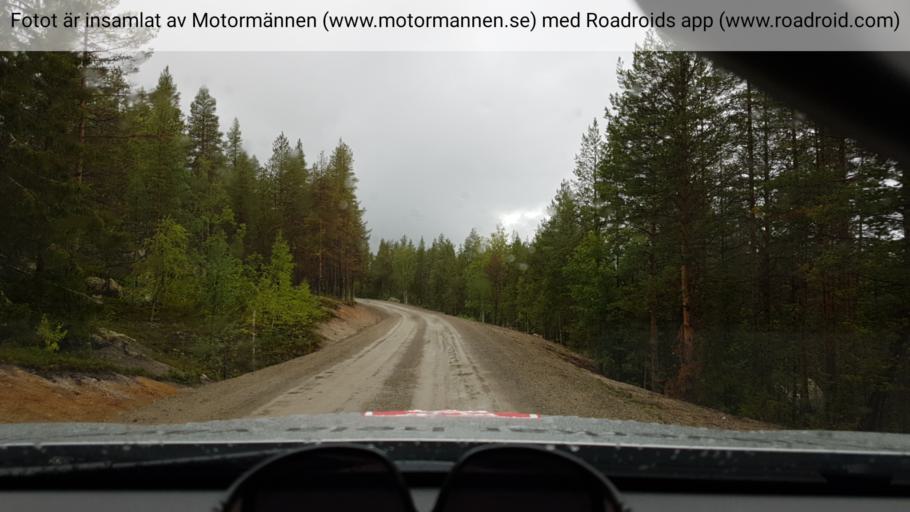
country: SE
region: Vaesterbotten
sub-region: Storumans Kommun
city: Storuman
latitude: 64.9552
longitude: 17.5527
